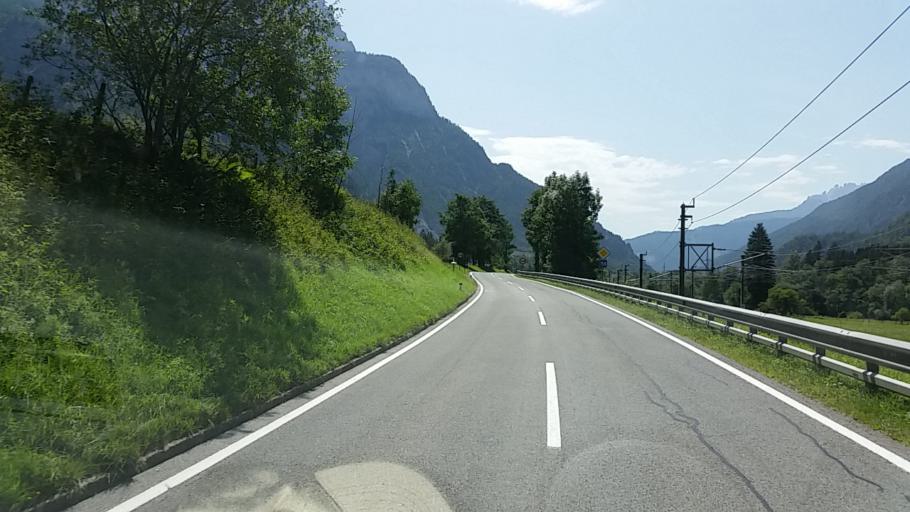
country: AT
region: Salzburg
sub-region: Politischer Bezirk Hallein
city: Golling an der Salzach
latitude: 47.5479
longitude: 13.1700
